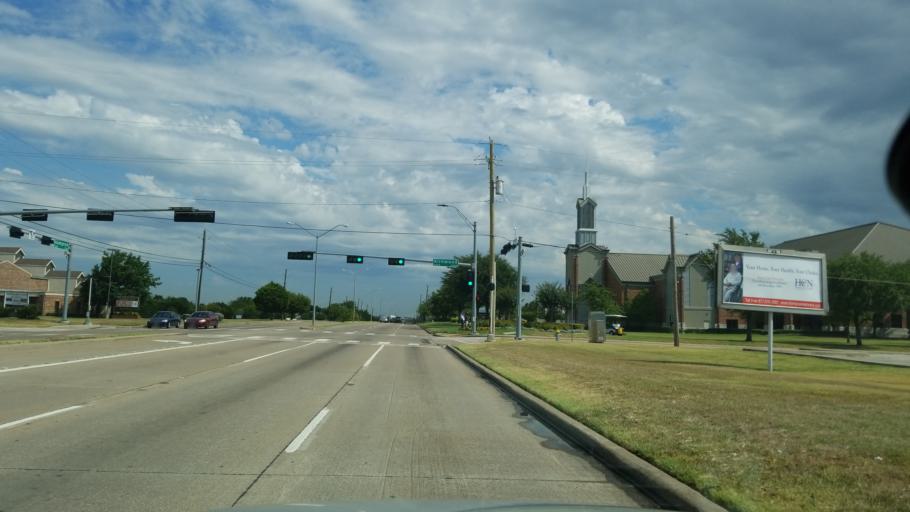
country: US
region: Texas
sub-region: Dallas County
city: Duncanville
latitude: 32.6544
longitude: -96.8570
